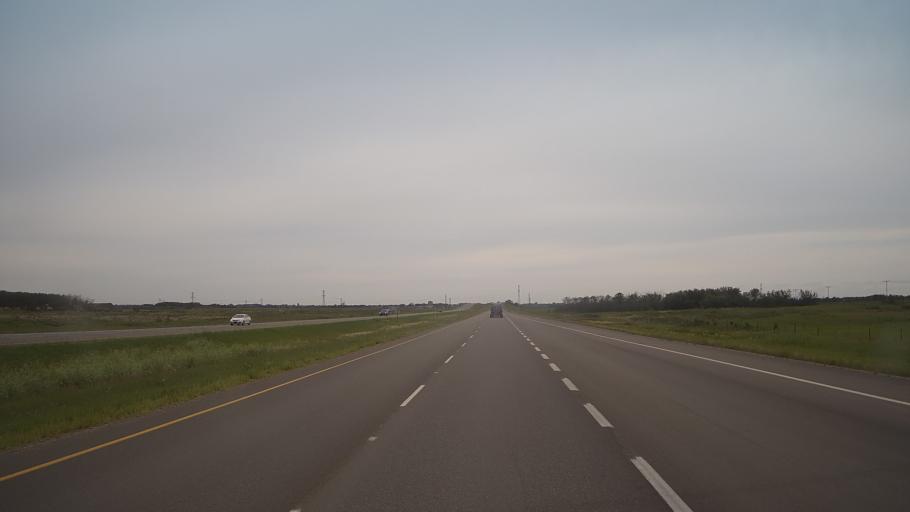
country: CA
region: Saskatchewan
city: Saskatoon
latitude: 52.0603
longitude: -106.6005
